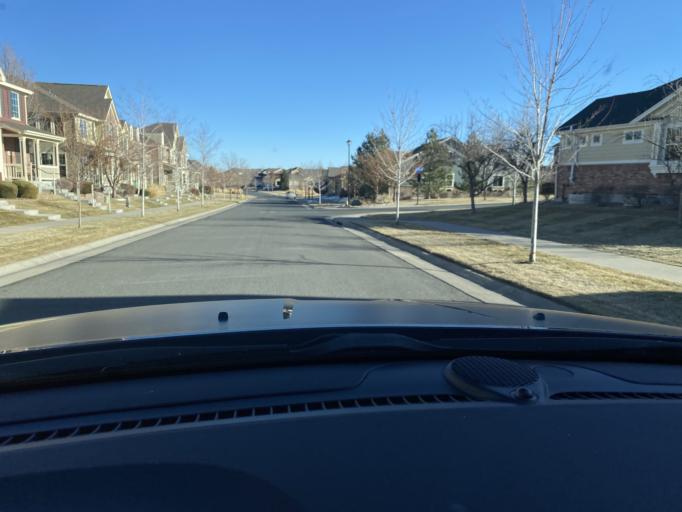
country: US
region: Colorado
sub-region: Jefferson County
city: Arvada
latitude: 39.8490
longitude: -105.1604
